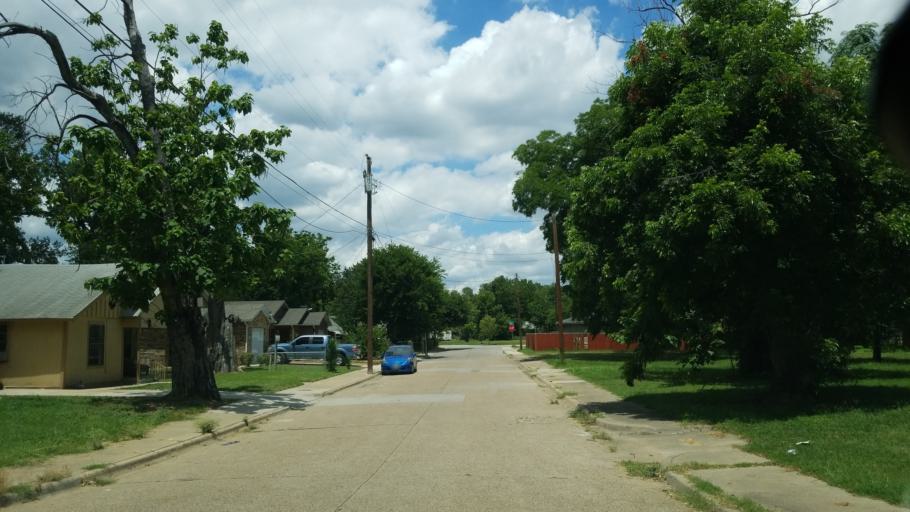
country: US
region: Texas
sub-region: Dallas County
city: Dallas
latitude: 32.7405
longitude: -96.7544
